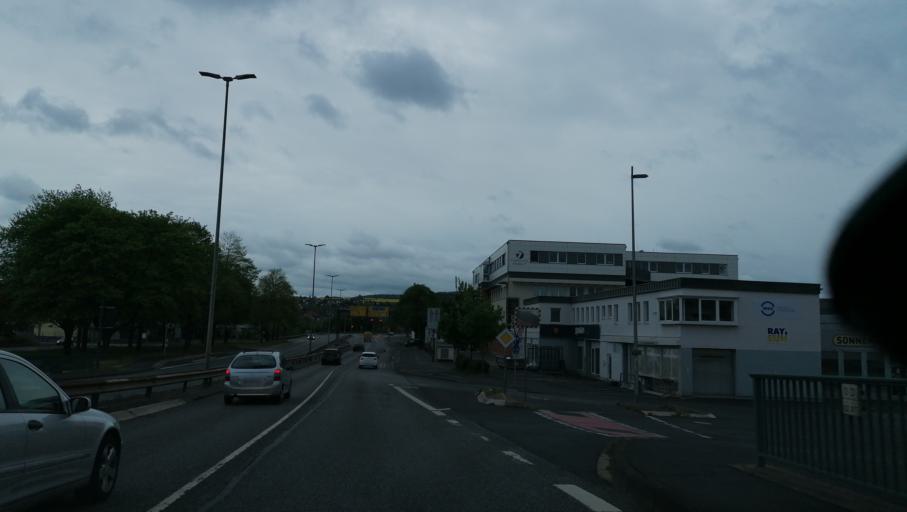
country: DE
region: Hesse
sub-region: Regierungsbezirk Kassel
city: Bad Hersfeld
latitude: 50.8657
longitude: 9.7166
